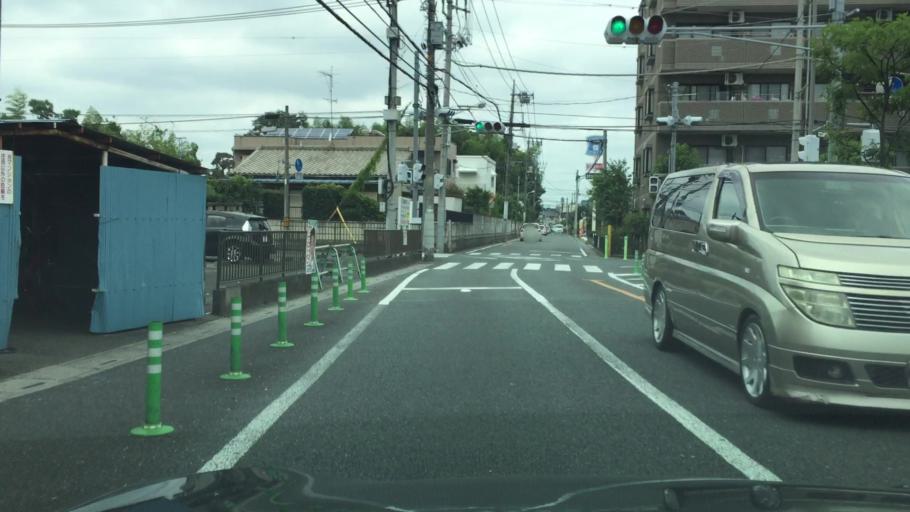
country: JP
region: Saitama
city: Ageoshimo
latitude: 35.9360
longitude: 139.6070
